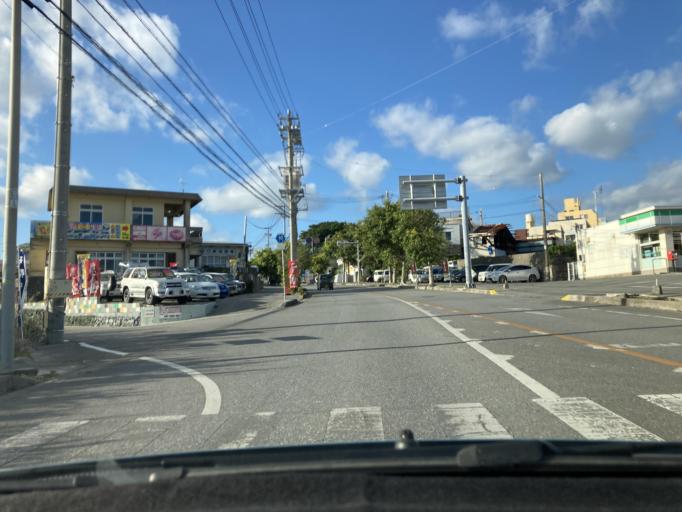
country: JP
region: Okinawa
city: Gushikawa
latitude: 26.3502
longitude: 127.8699
